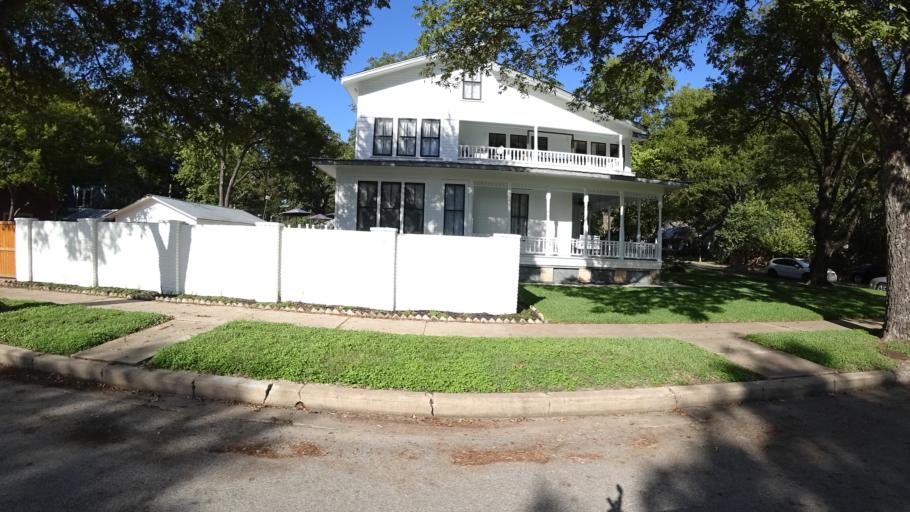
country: US
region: Texas
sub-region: Travis County
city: Austin
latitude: 30.3048
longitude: -97.7324
